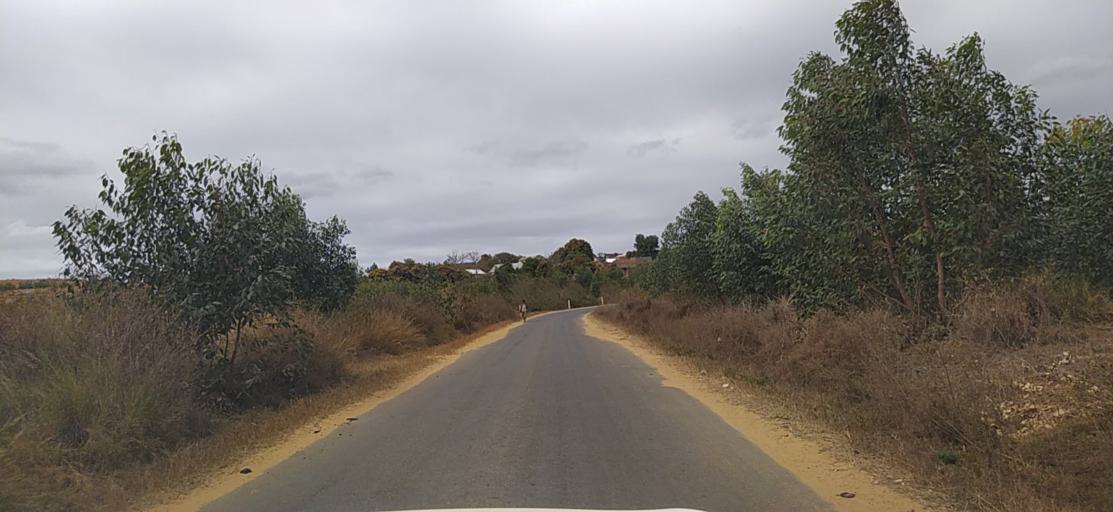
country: MG
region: Alaotra Mangoro
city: Ambatondrazaka
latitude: -17.9308
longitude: 48.2542
